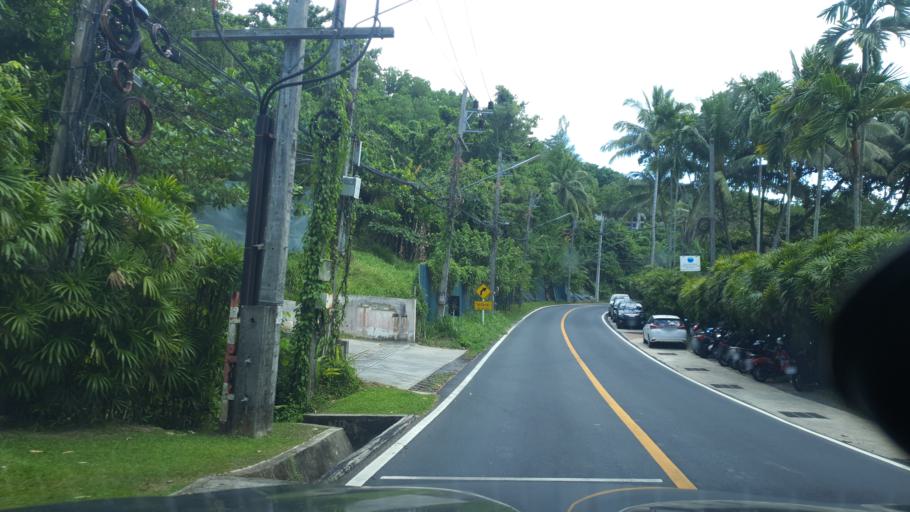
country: TH
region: Phuket
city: Thalang
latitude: 8.0508
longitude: 98.2777
